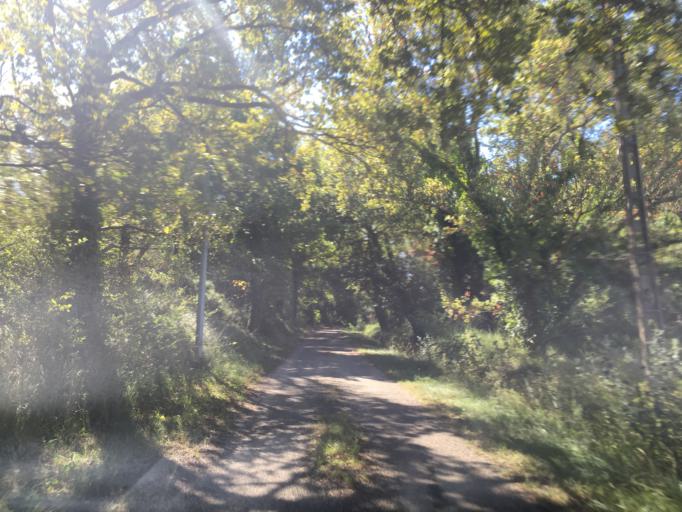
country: FR
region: Provence-Alpes-Cote d'Azur
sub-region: Departement du Vaucluse
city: Piolenc
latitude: 44.1483
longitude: 4.7682
